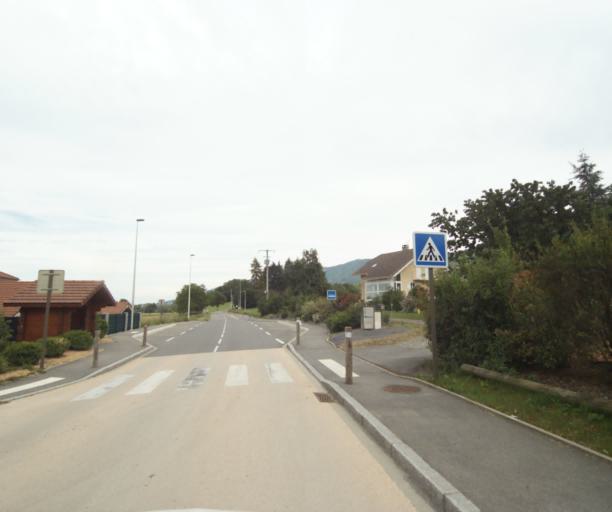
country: FR
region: Rhone-Alpes
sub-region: Departement de la Haute-Savoie
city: Bons-en-Chablais
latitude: 46.2680
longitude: 6.3960
